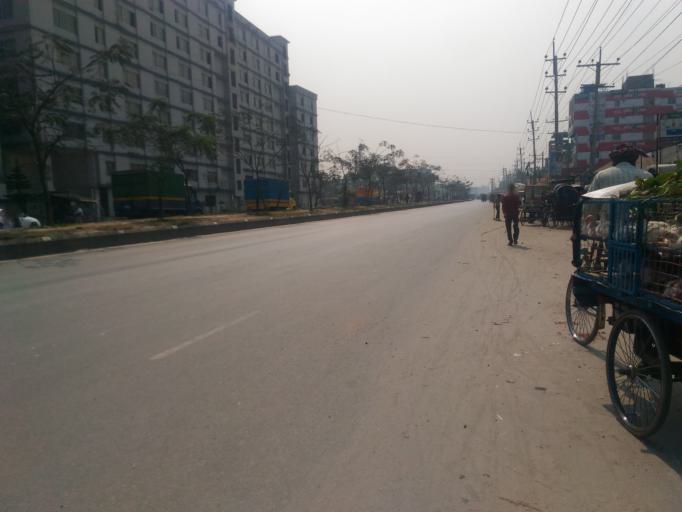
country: BD
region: Dhaka
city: Tungi
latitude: 24.0014
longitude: 90.3828
